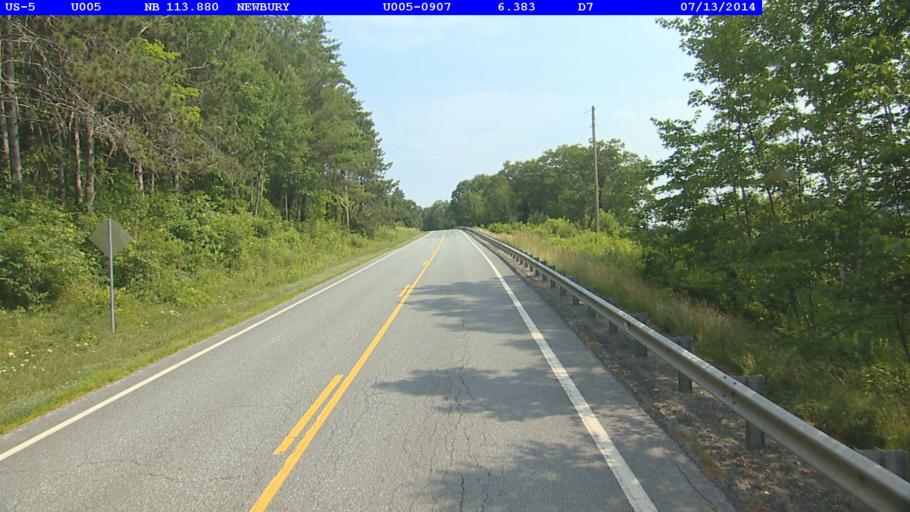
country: US
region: New Hampshire
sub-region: Grafton County
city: North Haverhill
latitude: 44.1121
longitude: -72.0558
